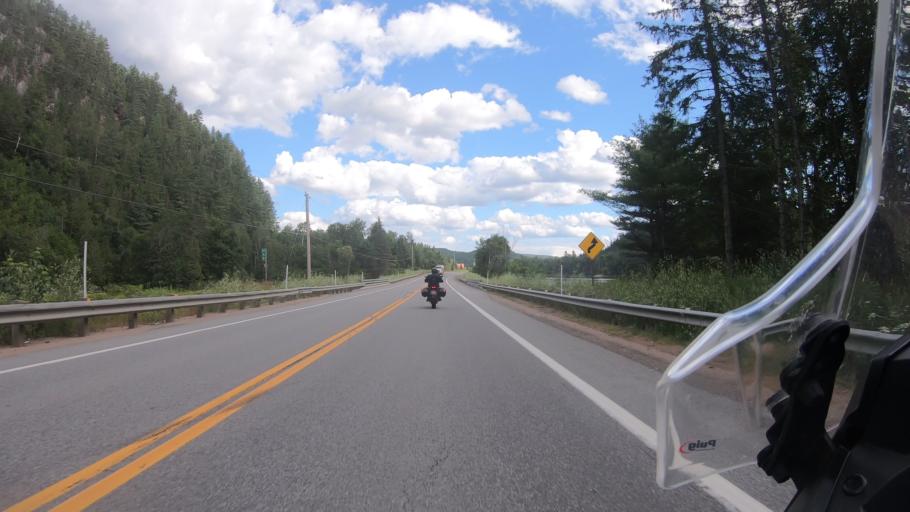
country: CA
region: Quebec
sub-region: Mauricie
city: Saint-Tite
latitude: 46.9893
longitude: -72.9126
